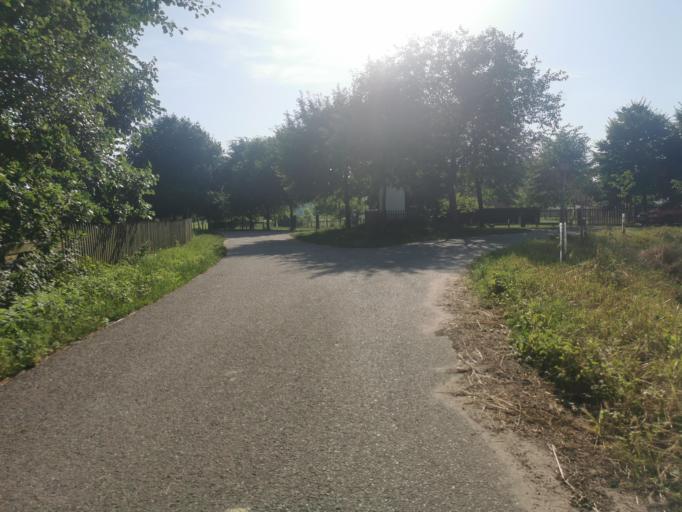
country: CZ
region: South Moravian
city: Ratiskovice
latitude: 48.9240
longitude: 17.1949
